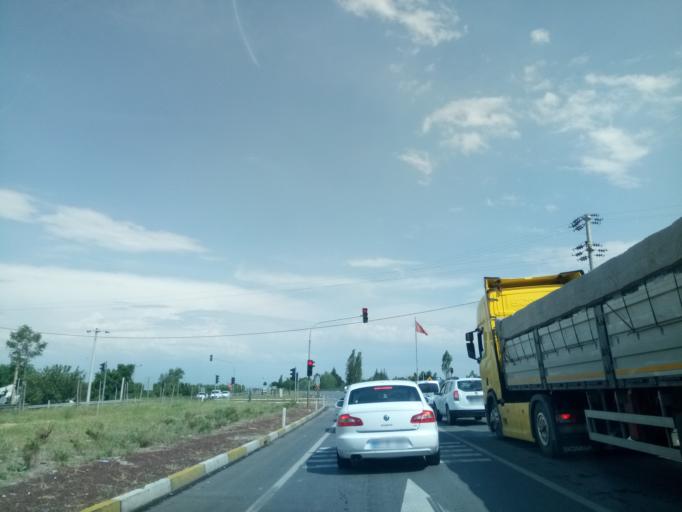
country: TR
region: Konya
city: Aksehir
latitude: 38.3931
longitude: 31.3811
